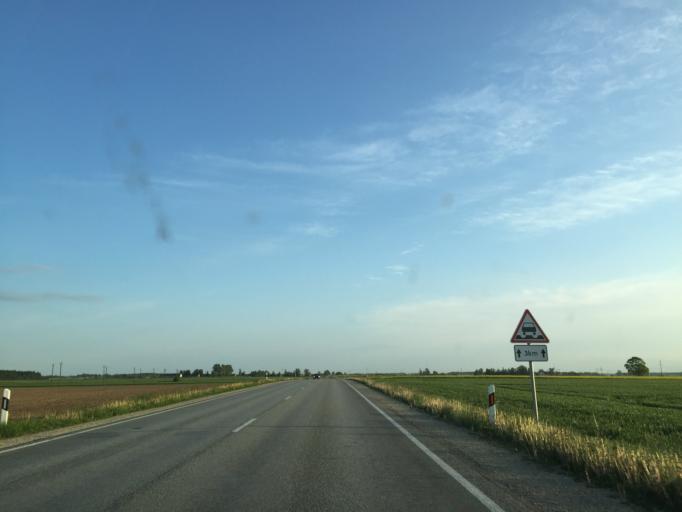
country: LT
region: Siauliu apskritis
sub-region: Joniskis
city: Joniskis
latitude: 56.1036
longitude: 23.4823
